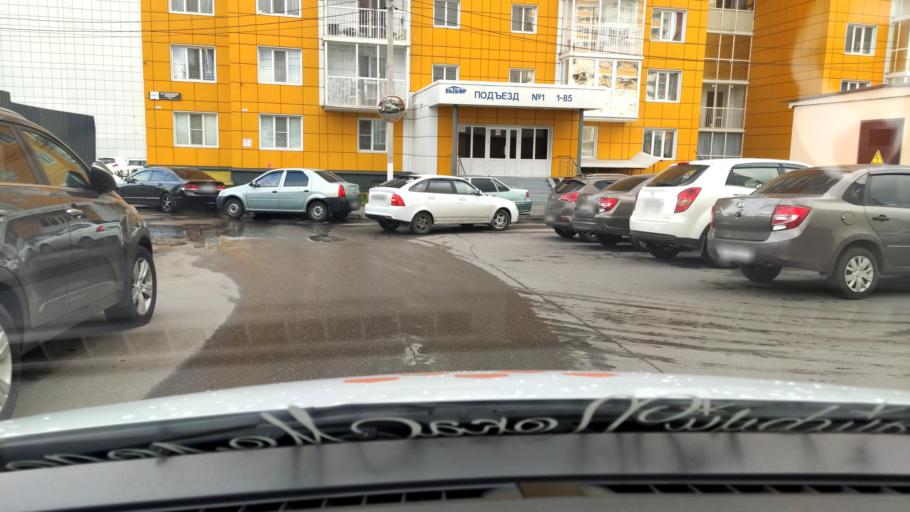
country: RU
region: Voronezj
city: Podgornoye
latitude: 51.6874
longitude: 39.1362
